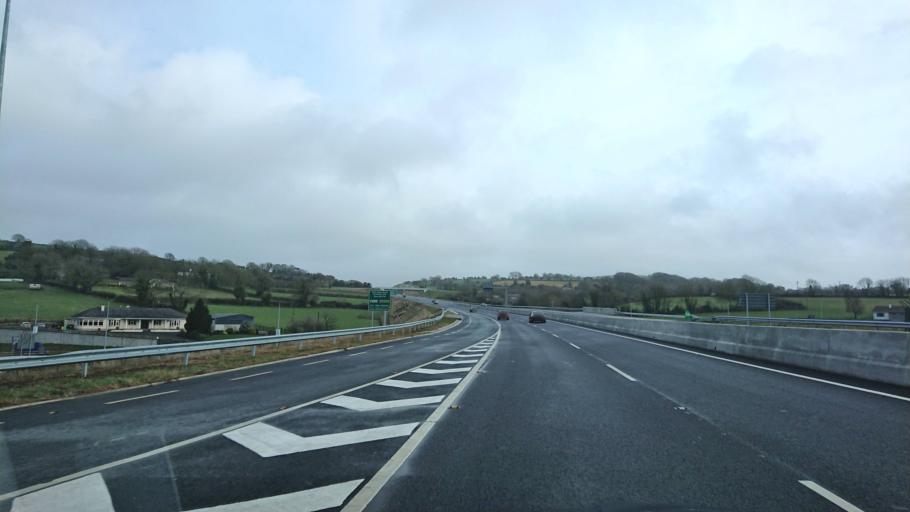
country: IE
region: Leinster
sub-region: Loch Garman
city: New Ross
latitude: 52.3622
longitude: -6.9615
